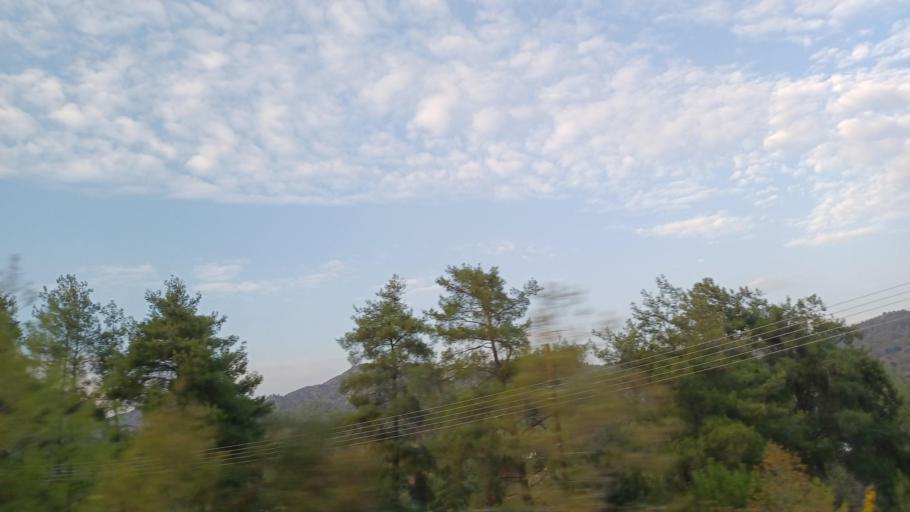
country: CY
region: Limassol
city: Pelendri
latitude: 34.8552
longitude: 32.9453
